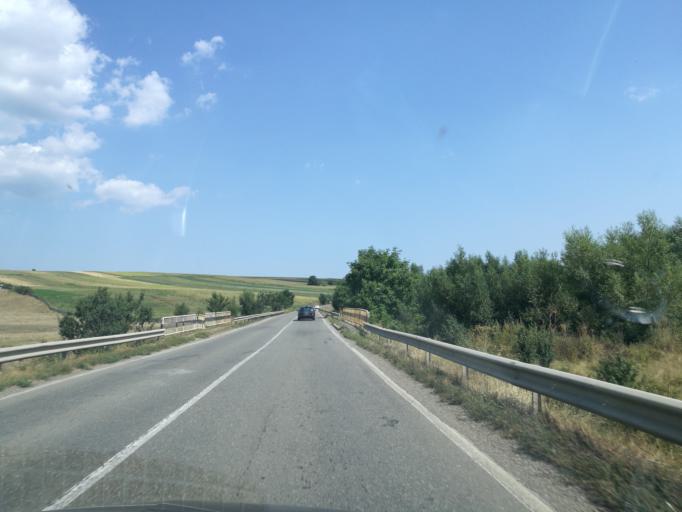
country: RO
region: Neamt
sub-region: Comuna Baltatesti
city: Valea Seaca
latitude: 47.1440
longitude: 26.3195
